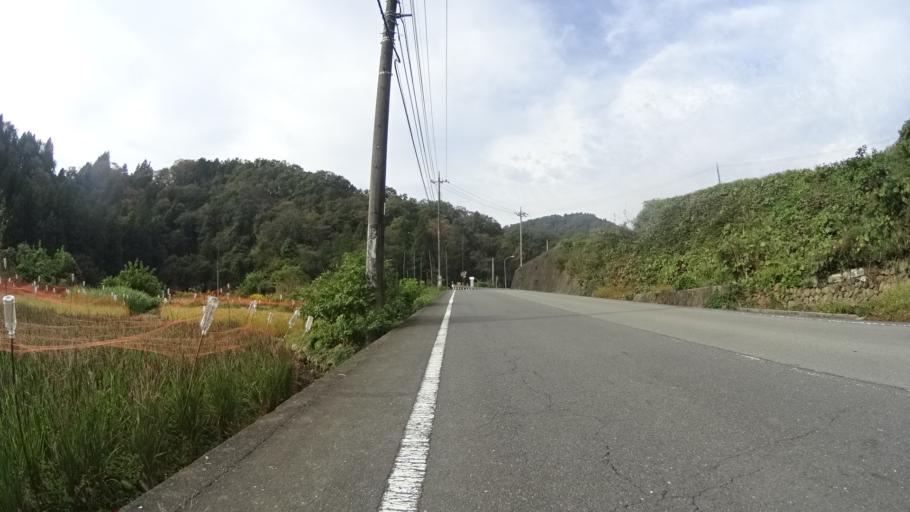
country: JP
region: Yamanashi
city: Uenohara
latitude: 35.6380
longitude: 139.0814
